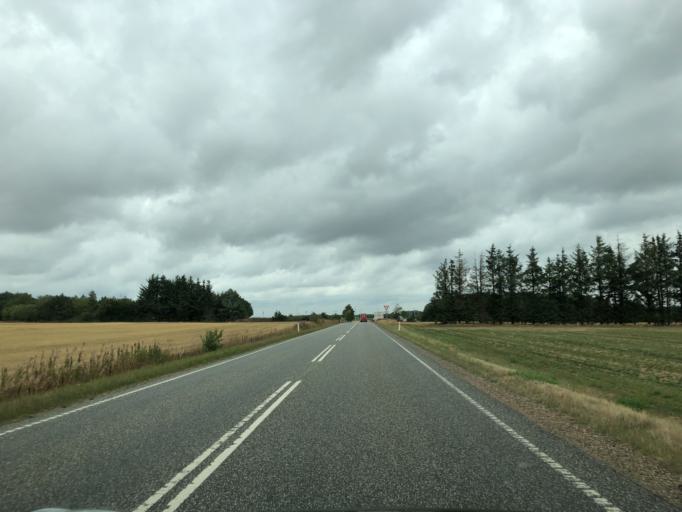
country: DK
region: Central Jutland
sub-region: Ringkobing-Skjern Kommune
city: Videbaek
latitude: 56.0825
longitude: 8.5071
